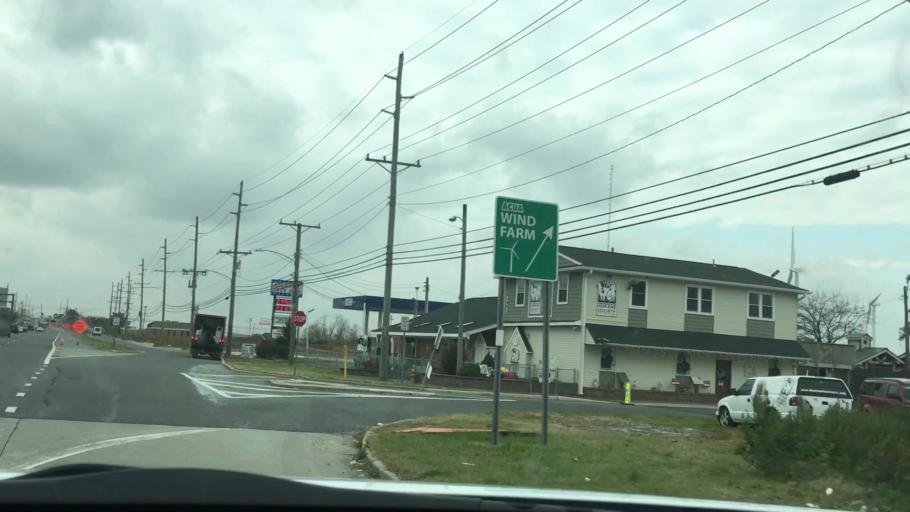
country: US
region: New Jersey
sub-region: Atlantic County
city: Atlantic City
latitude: 39.3750
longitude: -74.4441
